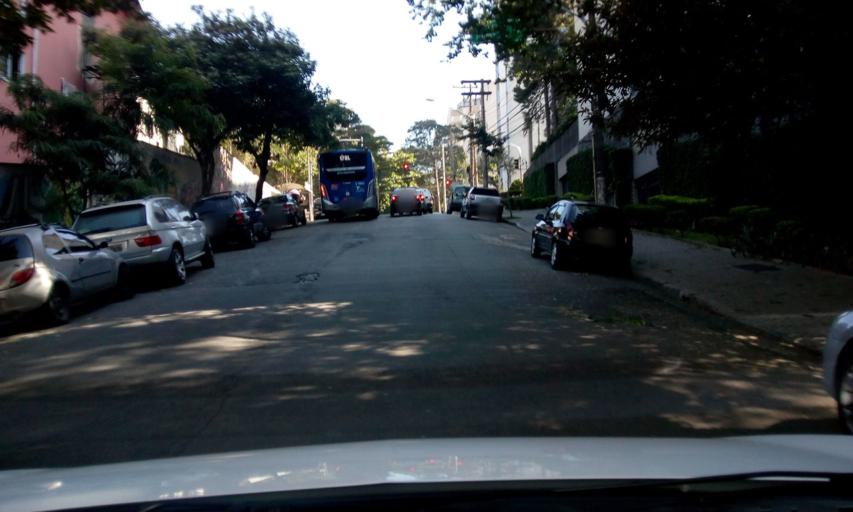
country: BR
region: Sao Paulo
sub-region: Sao Paulo
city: Sao Paulo
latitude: -23.5473
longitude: -46.6863
